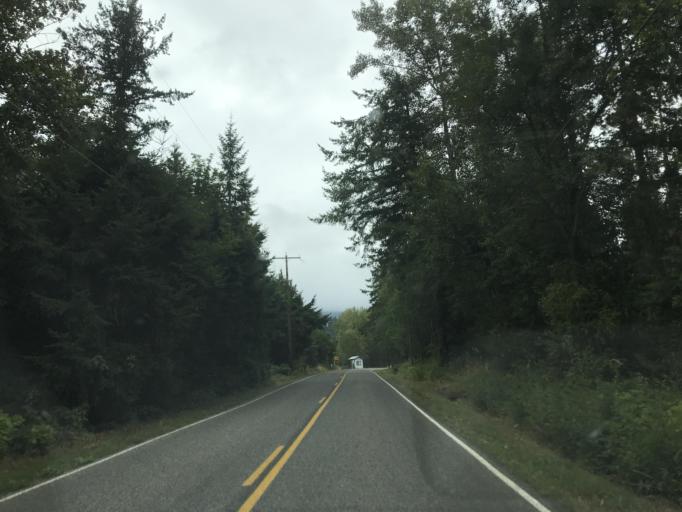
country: US
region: Washington
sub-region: Whatcom County
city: Sudden Valley
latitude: 48.7995
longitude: -122.3340
